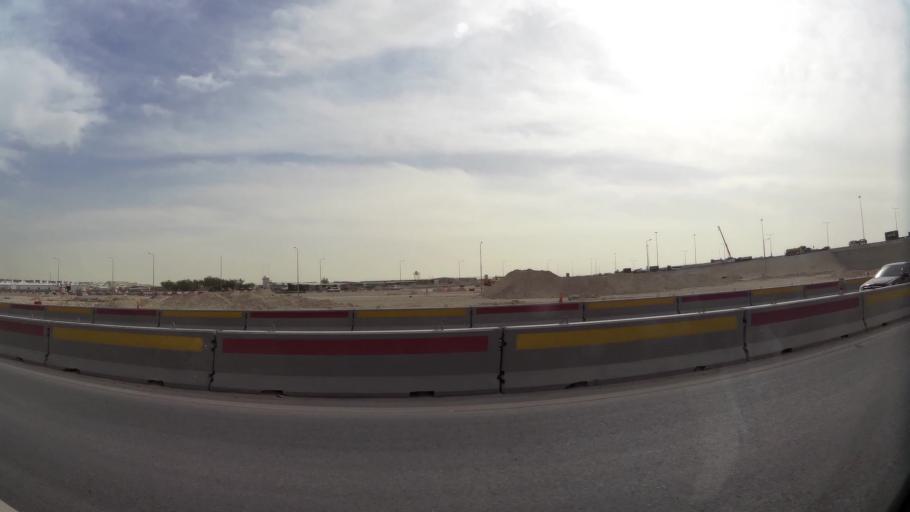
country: QA
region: Baladiyat ar Rayyan
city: Ar Rayyan
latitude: 25.3296
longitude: 51.3346
